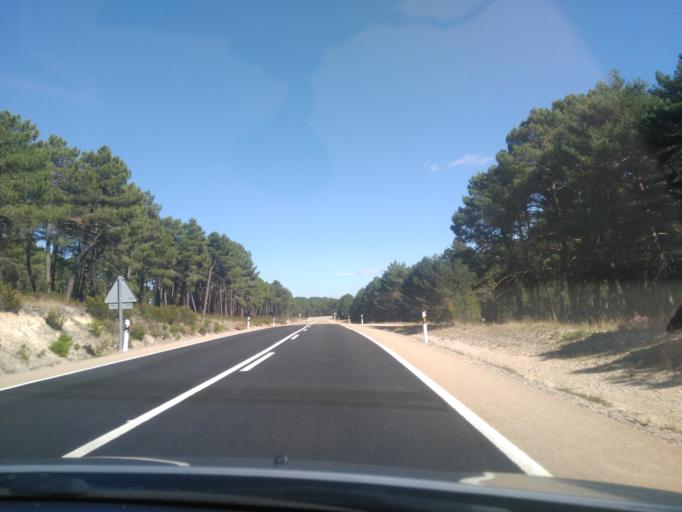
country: ES
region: Castille and Leon
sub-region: Provincia de Soria
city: Navaleno
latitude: 41.8365
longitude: -3.0047
